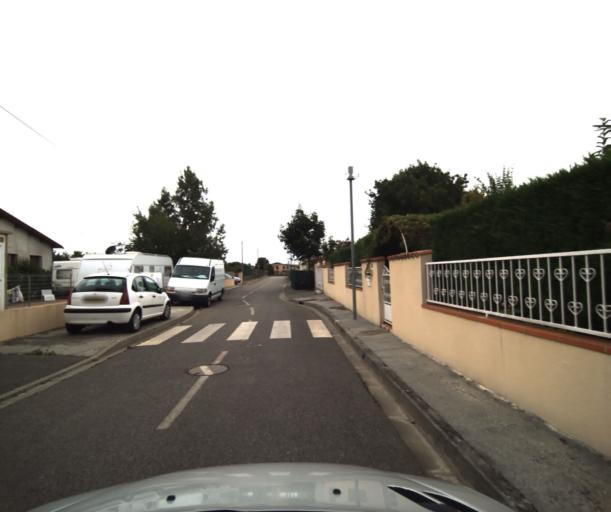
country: FR
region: Midi-Pyrenees
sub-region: Departement de la Haute-Garonne
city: Portet-sur-Garonne
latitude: 43.5387
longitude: 1.3956
